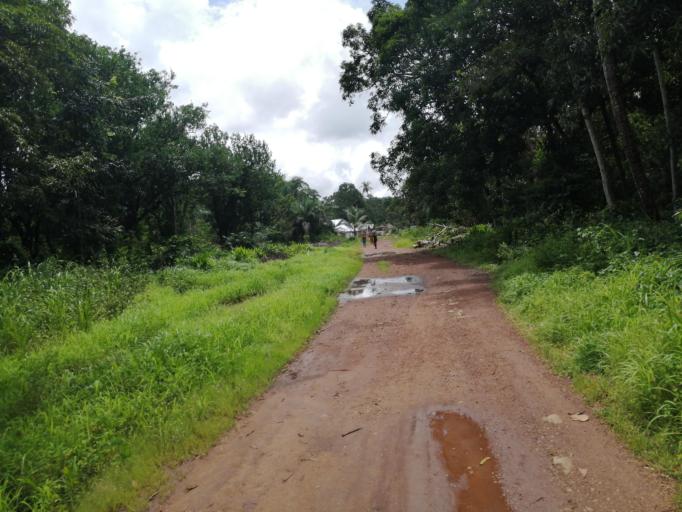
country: SL
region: Northern Province
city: Port Loko
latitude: 8.7894
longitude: -12.7733
